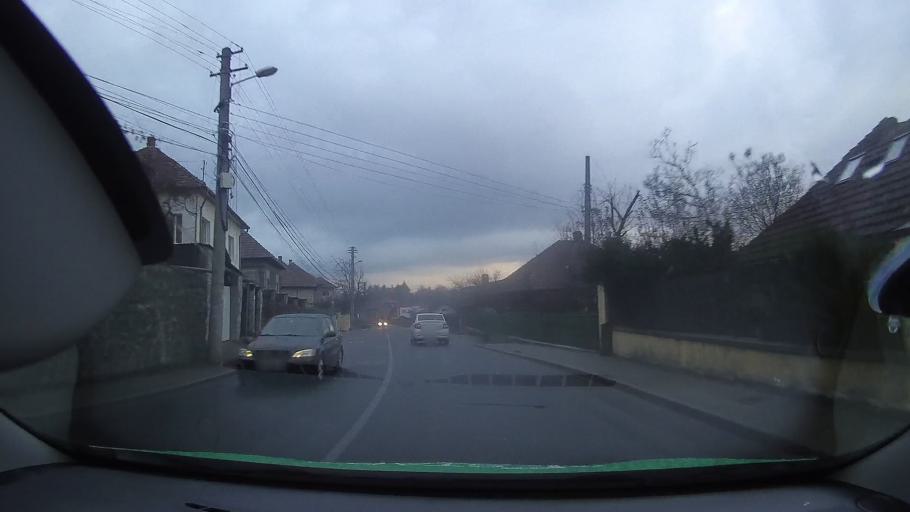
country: RO
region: Hunedoara
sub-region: Municipiul Brad
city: Brad
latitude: 46.1267
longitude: 22.7865
